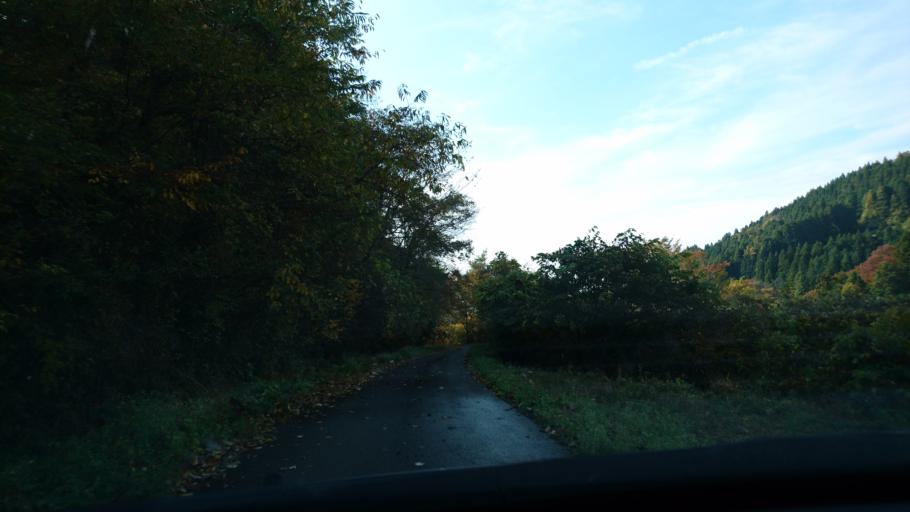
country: JP
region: Iwate
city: Ichinoseki
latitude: 38.9820
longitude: 141.1765
